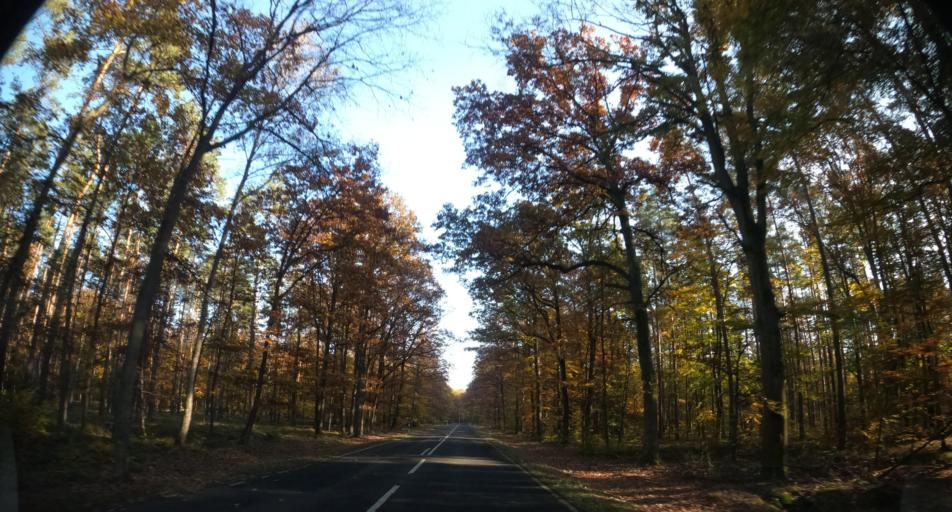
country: PL
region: West Pomeranian Voivodeship
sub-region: Powiat policki
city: Nowe Warpno
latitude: 53.6114
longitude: 14.3109
